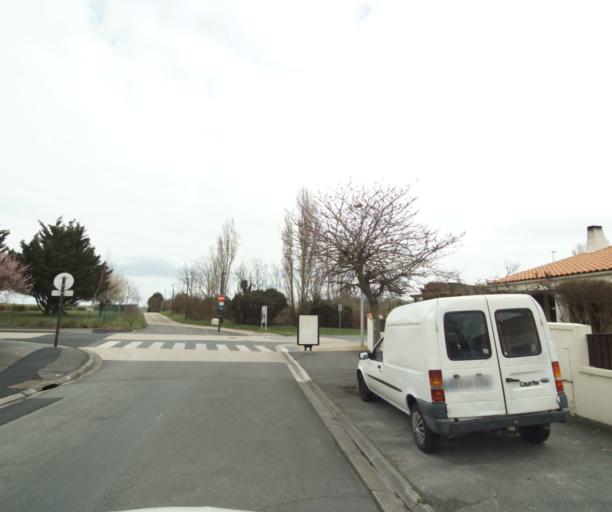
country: FR
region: Poitou-Charentes
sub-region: Departement de la Charente-Maritime
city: Lagord
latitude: 46.1905
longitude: -1.1481
